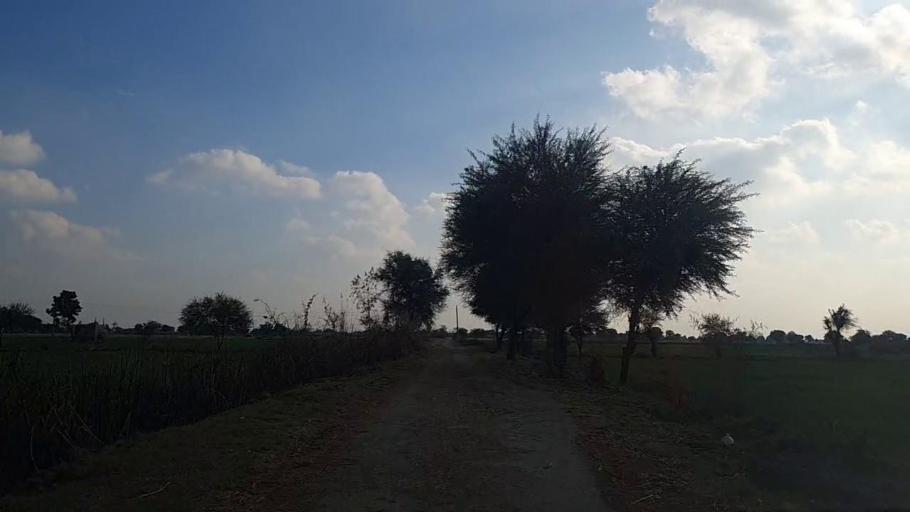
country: PK
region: Sindh
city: Tando Mittha Khan
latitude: 25.9443
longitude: 69.2148
